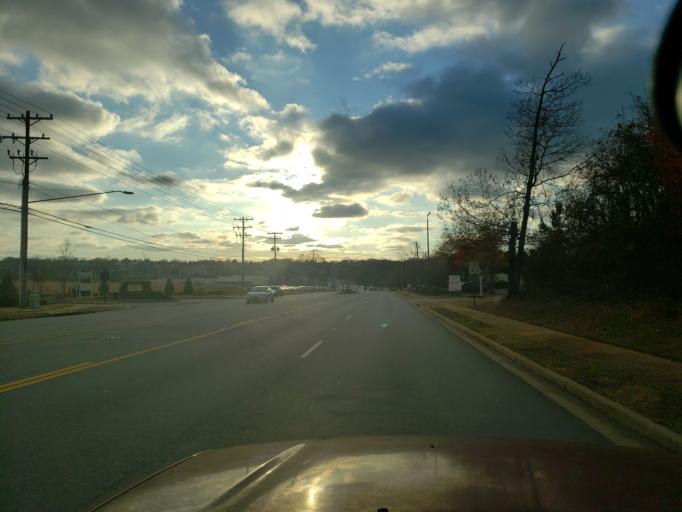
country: US
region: South Carolina
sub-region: Greenville County
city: Greenville
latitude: 34.8346
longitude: -82.3389
